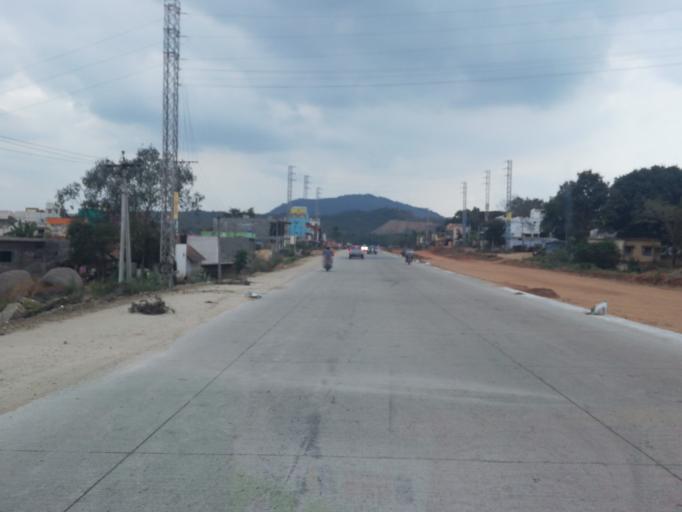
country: IN
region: Andhra Pradesh
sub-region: Chittoor
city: Ramapuram
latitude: 13.1025
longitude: 79.1247
